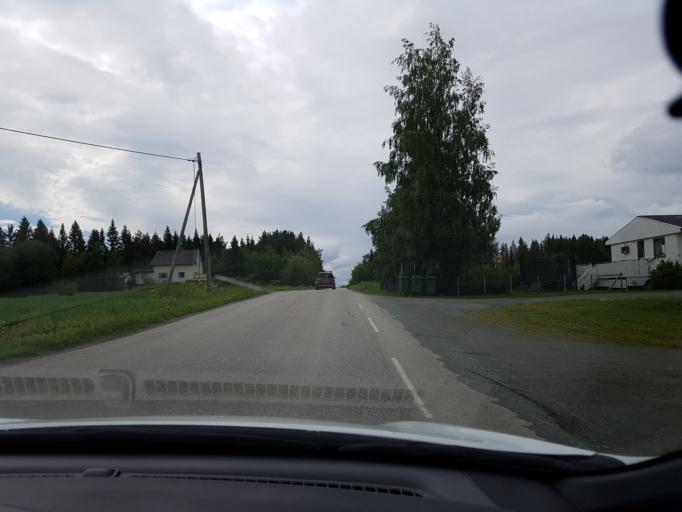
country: NO
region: Nord-Trondelag
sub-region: Frosta
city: Frosta
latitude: 63.6051
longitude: 10.7359
